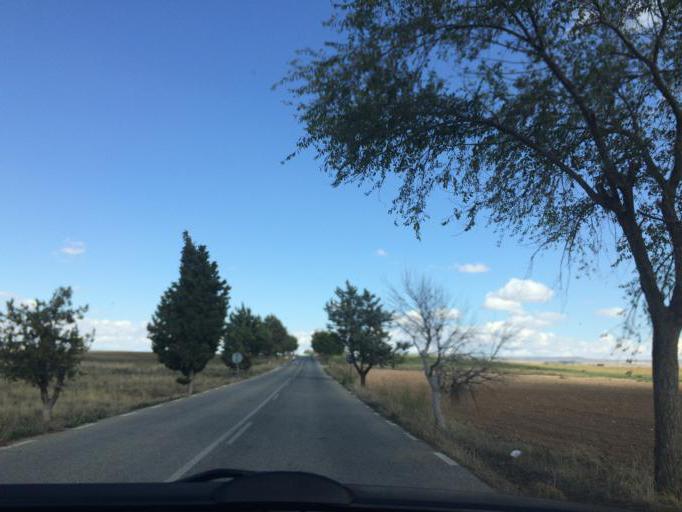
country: ES
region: Castille-La Mancha
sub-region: Provincia de Albacete
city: Albacete
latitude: 38.9598
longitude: -1.8364
